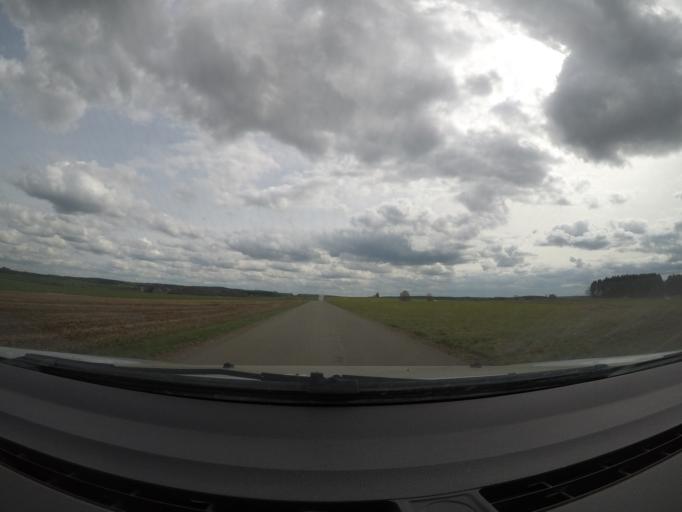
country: BE
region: Wallonia
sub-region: Province du Luxembourg
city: Leglise
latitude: 49.7890
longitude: 5.5393
